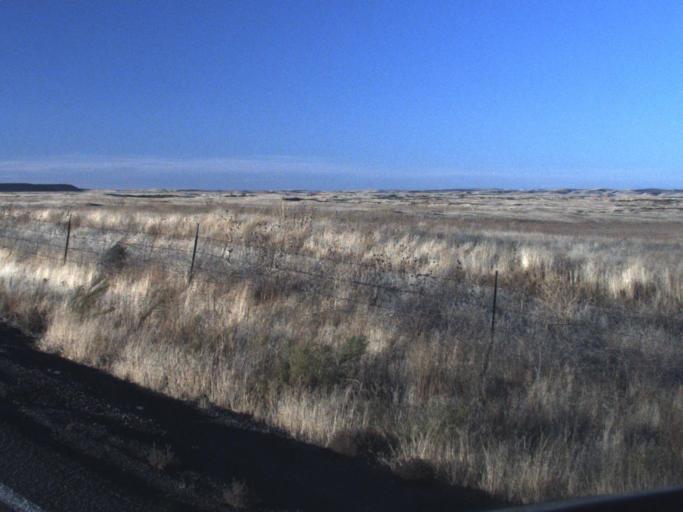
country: US
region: Washington
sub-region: Walla Walla County
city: Waitsburg
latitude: 46.6589
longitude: -118.2685
